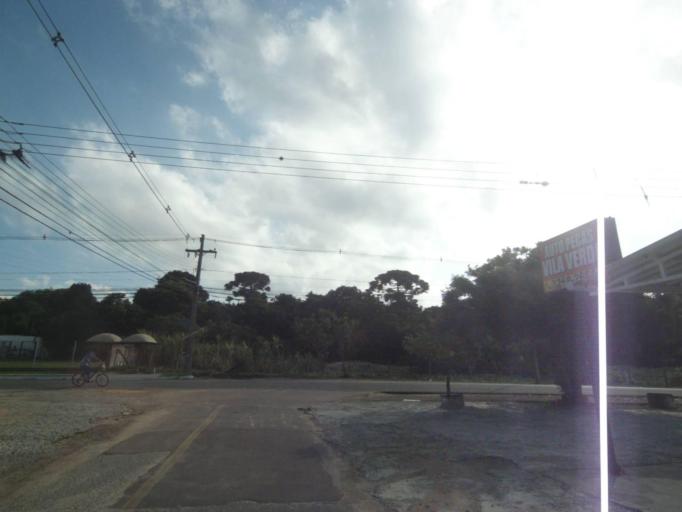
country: BR
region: Parana
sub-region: Araucaria
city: Araucaria
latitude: -25.5345
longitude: -49.3327
